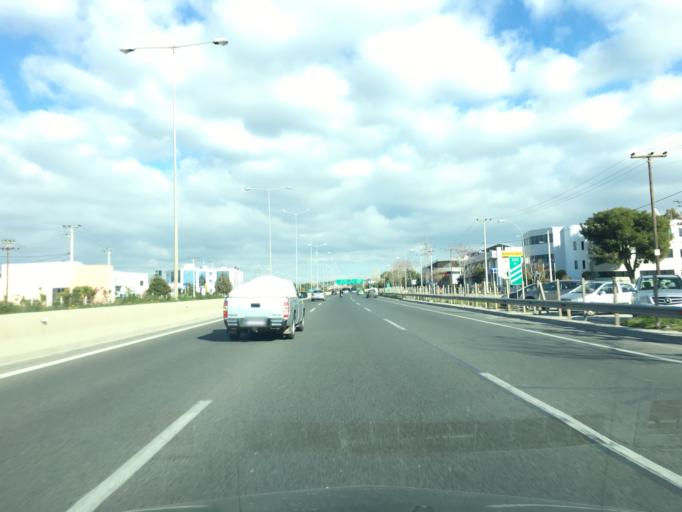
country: GR
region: Attica
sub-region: Nomarchia Athinas
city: Nea Erythraia
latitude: 38.1006
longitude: 23.8063
